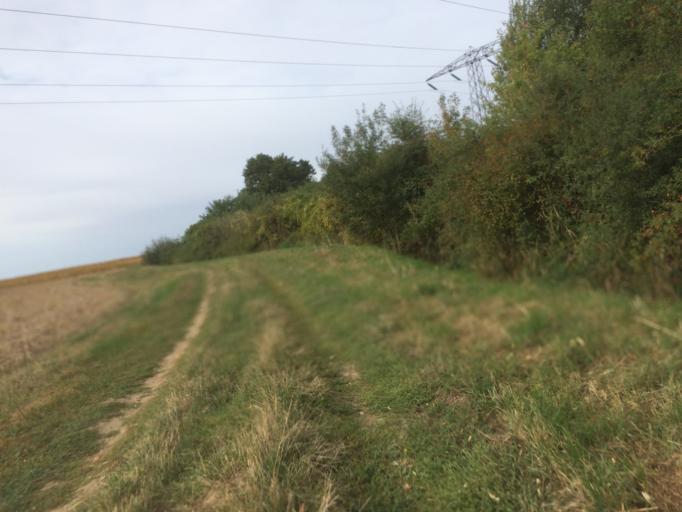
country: FR
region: Ile-de-France
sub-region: Departement de l'Essonne
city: Gometz-la-Ville
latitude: 48.6680
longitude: 2.1221
